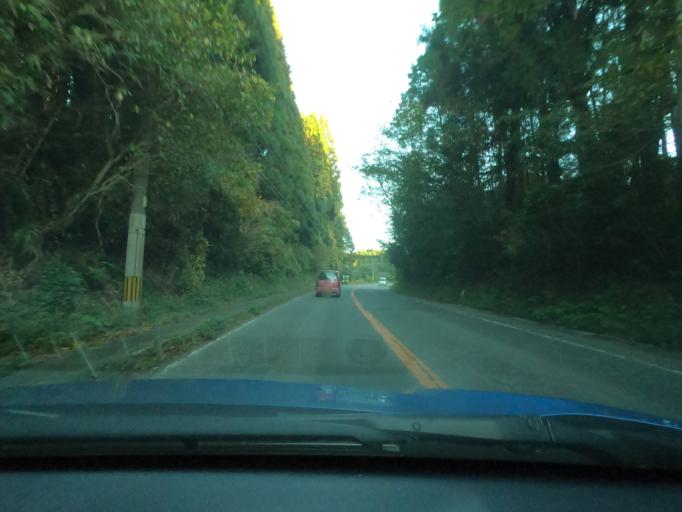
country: JP
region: Kagoshima
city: Satsumasendai
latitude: 31.8134
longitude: 130.3767
